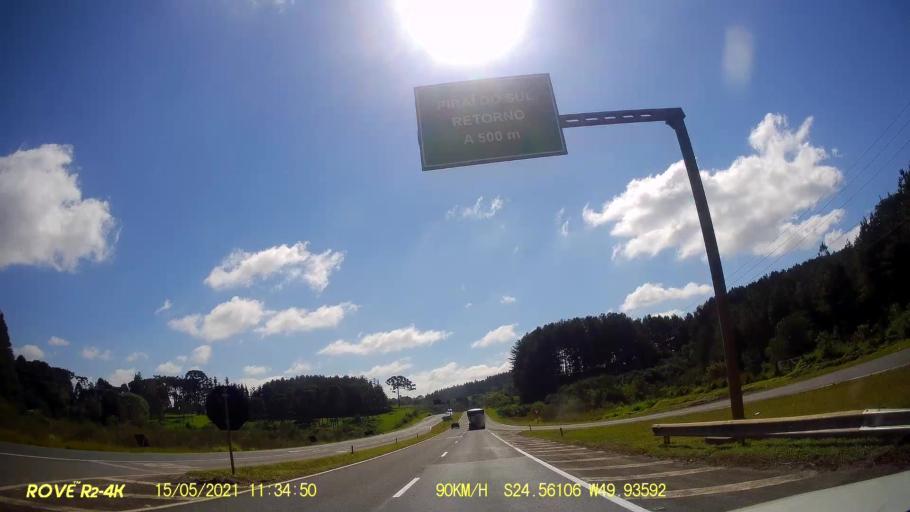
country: BR
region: Parana
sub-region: Pirai Do Sul
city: Pirai do Sul
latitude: -24.5611
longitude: -49.9359
